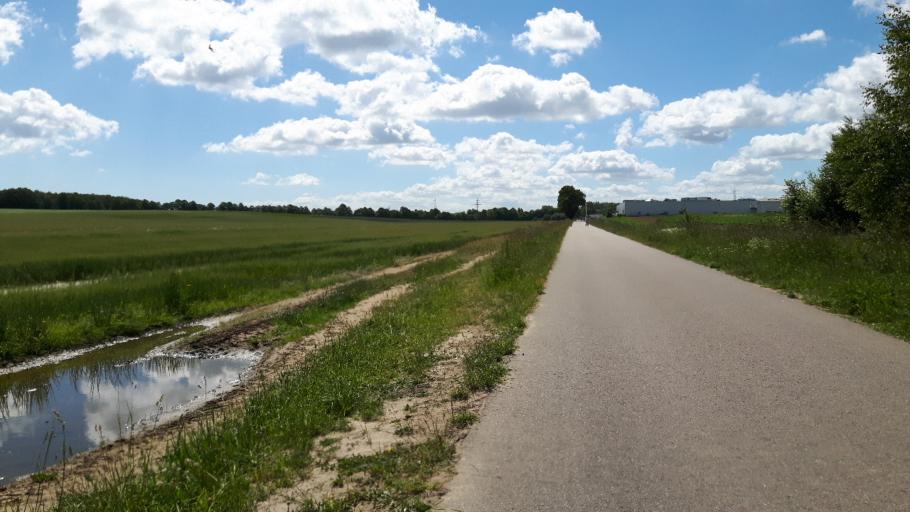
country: PL
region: Pomeranian Voivodeship
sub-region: Gdynia
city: Pogorze
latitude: 54.5699
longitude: 18.5017
